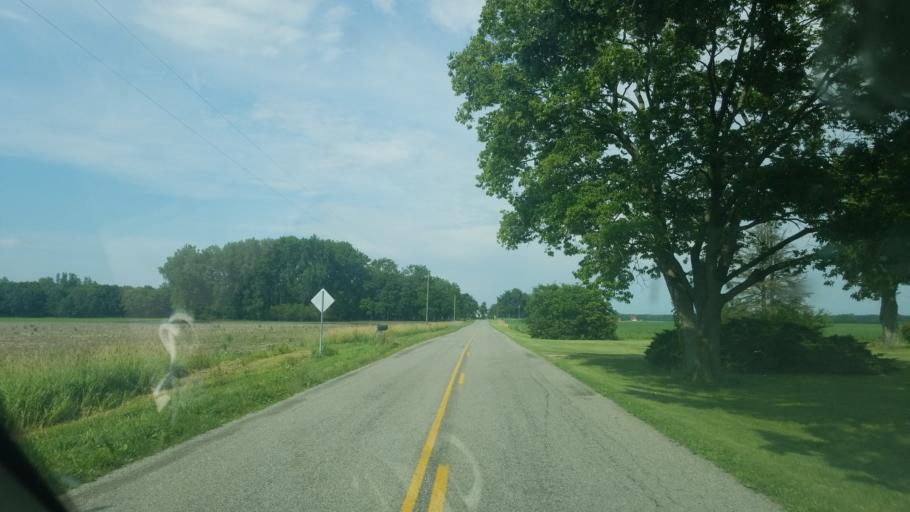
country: US
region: Ohio
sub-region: Champaign County
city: North Lewisburg
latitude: 40.1783
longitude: -83.4789
